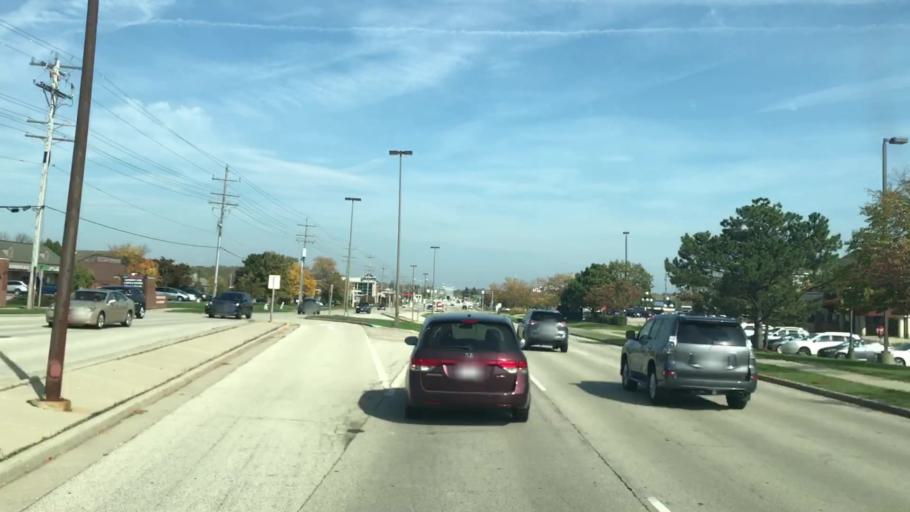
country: US
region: Wisconsin
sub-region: Milwaukee County
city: River Hills
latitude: 43.2185
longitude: -87.9240
